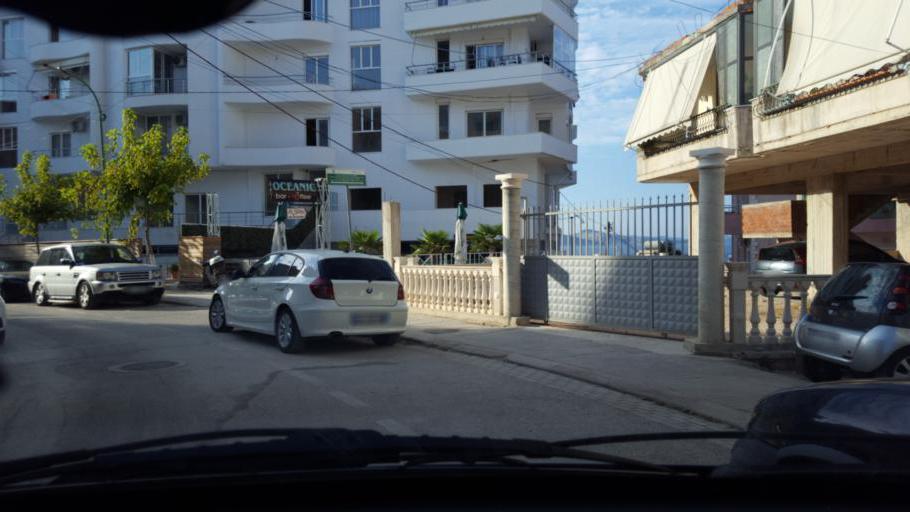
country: AL
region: Vlore
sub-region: Rrethi i Sarandes
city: Sarande
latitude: 39.8691
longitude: 19.9996
